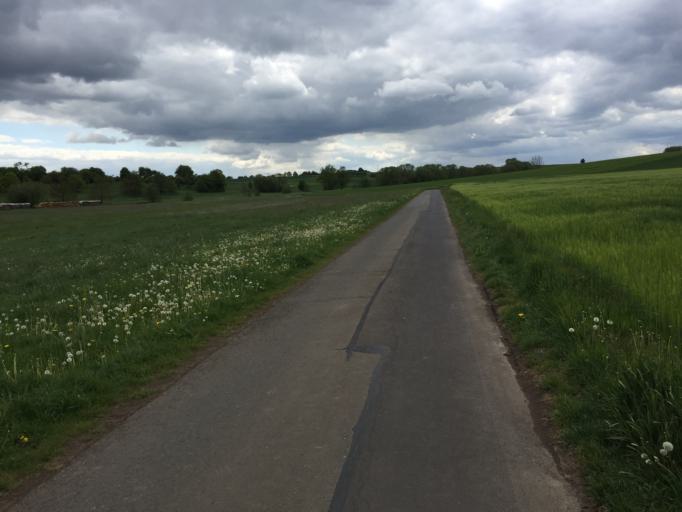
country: DE
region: Hesse
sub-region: Regierungsbezirk Giessen
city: Grunberg
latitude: 50.5745
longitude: 8.9227
